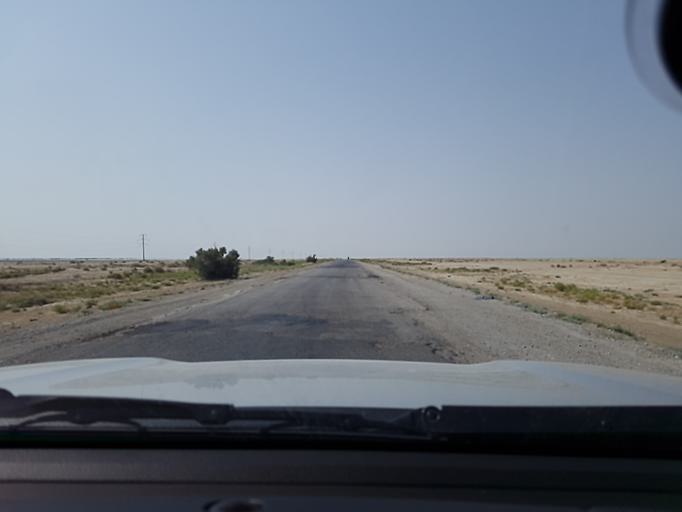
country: TM
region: Balkan
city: Gumdag
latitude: 38.8821
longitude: 54.5934
